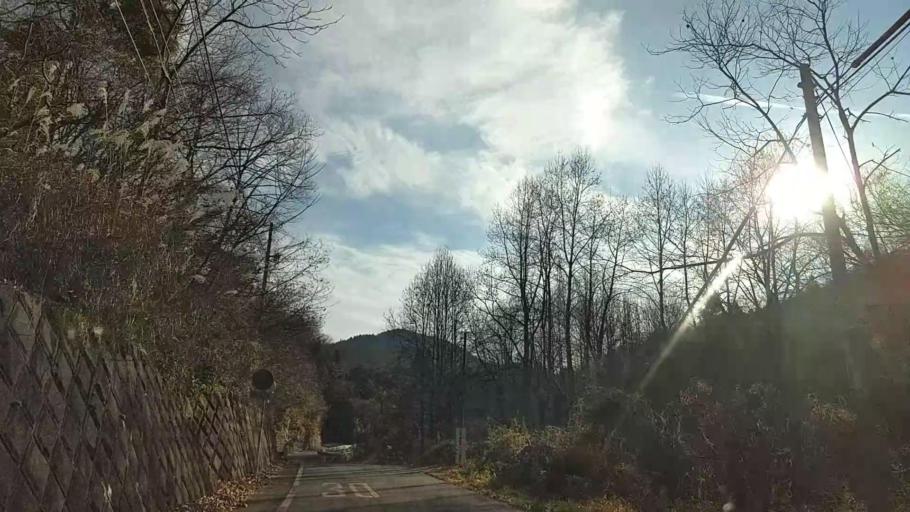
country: JP
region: Yamanashi
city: Uenohara
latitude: 35.5611
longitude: 139.2064
